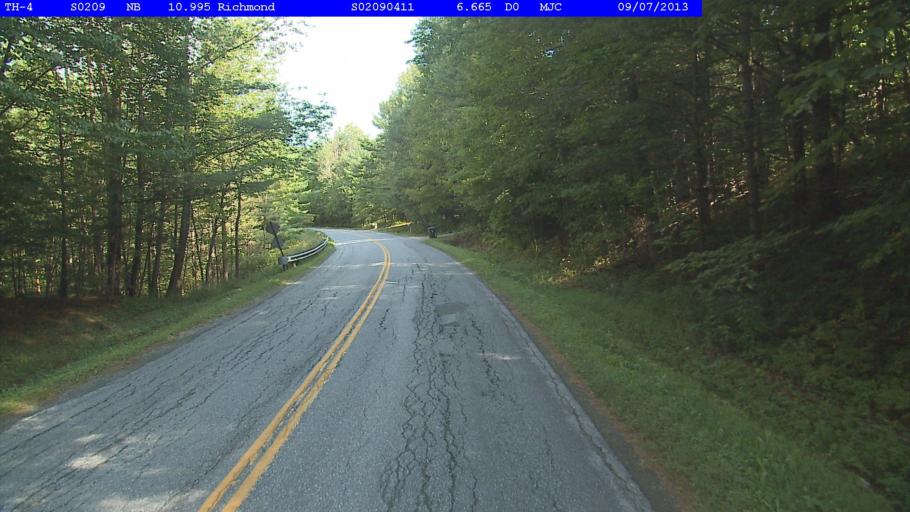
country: US
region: Vermont
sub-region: Chittenden County
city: Jericho
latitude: 44.4206
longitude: -72.9785
